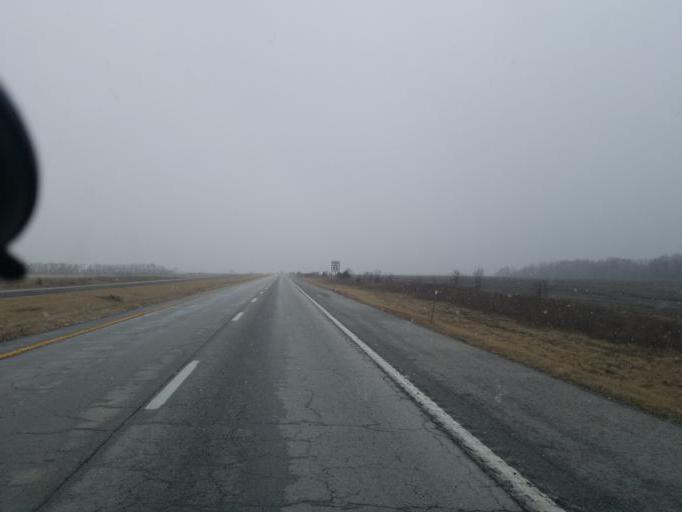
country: US
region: Missouri
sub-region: Macon County
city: La Plata
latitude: 39.9501
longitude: -92.4770
